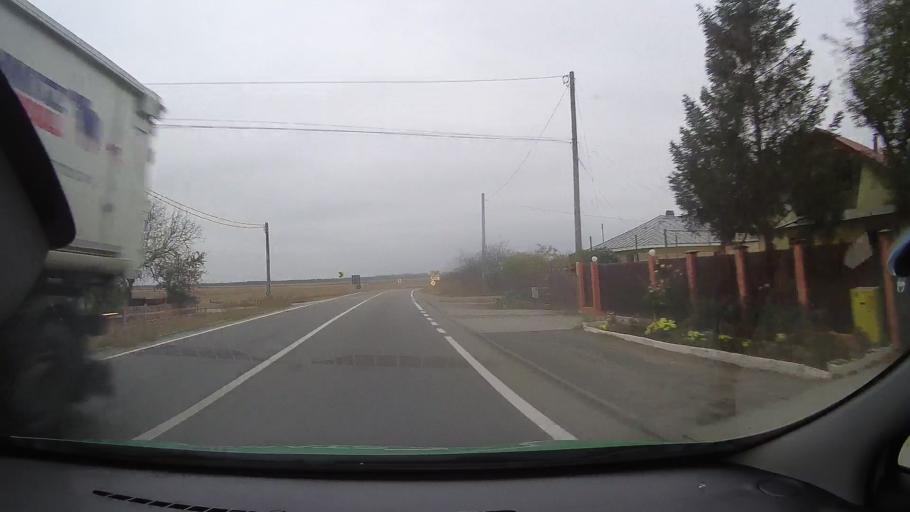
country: RO
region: Ialomita
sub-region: Comuna Slobozia
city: Slobozia
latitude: 44.5958
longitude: 27.3907
